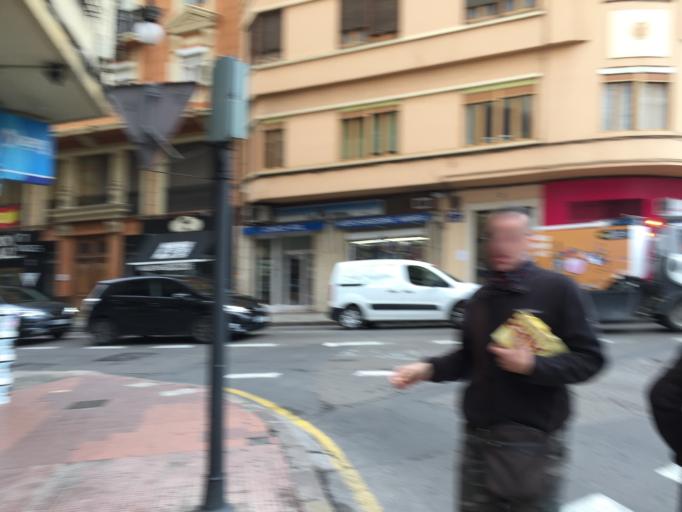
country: ES
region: Valencia
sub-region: Provincia de Valencia
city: Valencia
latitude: 39.4674
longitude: -0.3828
